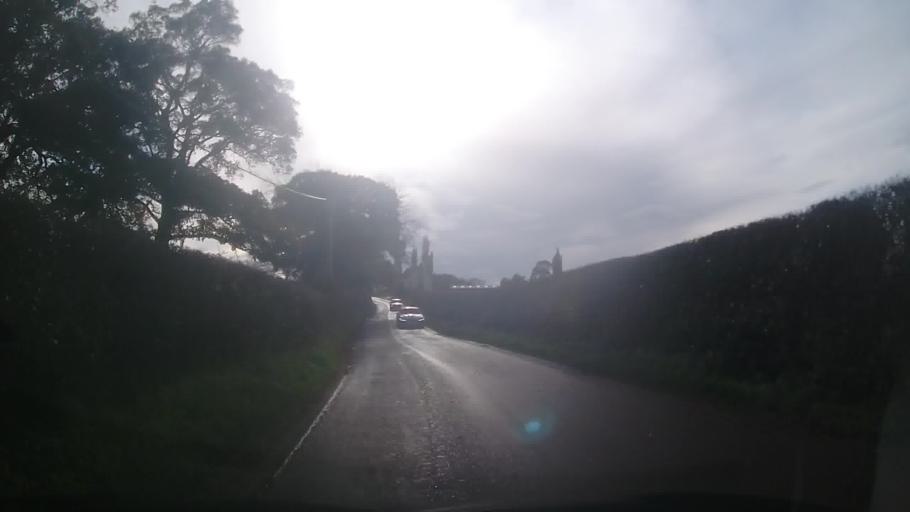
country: GB
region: England
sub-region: Shropshire
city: Whitchurch
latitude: 52.9564
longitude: -2.6955
